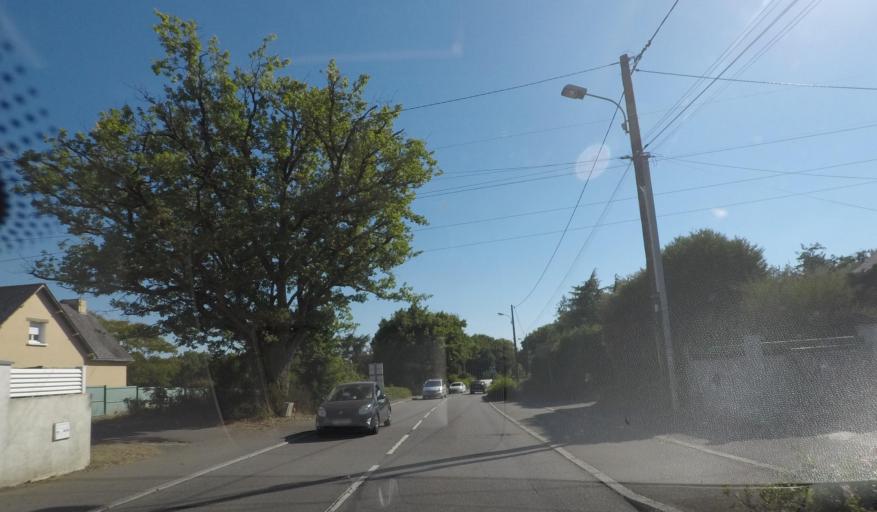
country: FR
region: Pays de la Loire
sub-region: Departement de la Loire-Atlantique
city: Pontchateau
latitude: 47.4287
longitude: -2.0856
